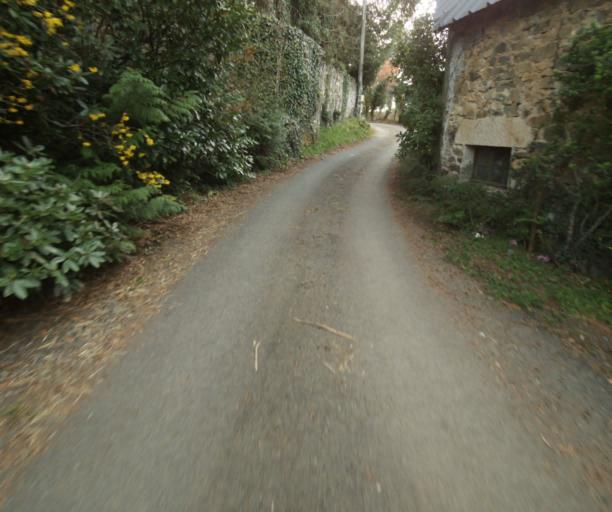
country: FR
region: Limousin
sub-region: Departement de la Correze
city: Naves
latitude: 45.3260
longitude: 1.7596
